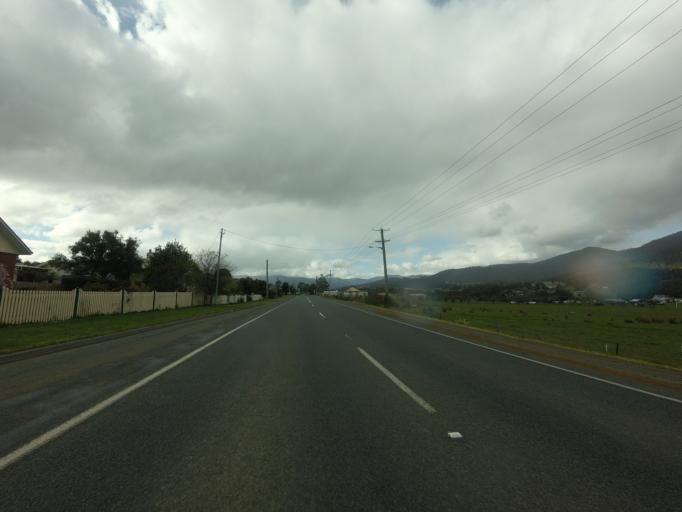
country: AU
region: Tasmania
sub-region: Huon Valley
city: Huonville
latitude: -43.0392
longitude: 147.0455
